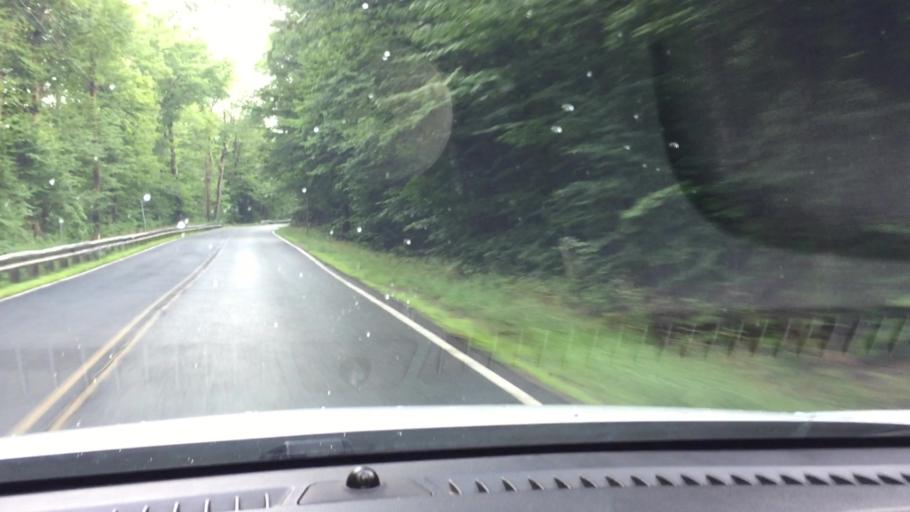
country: US
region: Massachusetts
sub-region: Berkshire County
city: Becket
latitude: 42.4219
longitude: -72.9924
